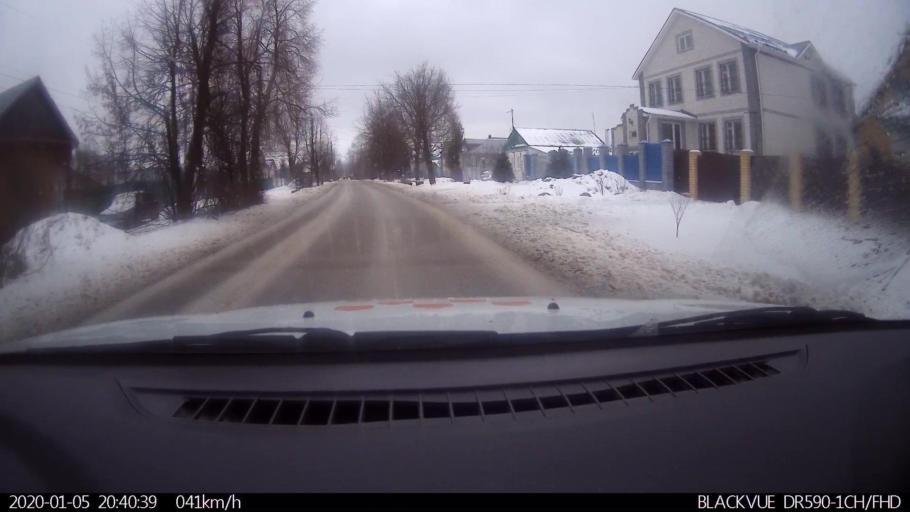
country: RU
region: Nizjnij Novgorod
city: Lukino
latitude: 56.4085
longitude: 43.7284
